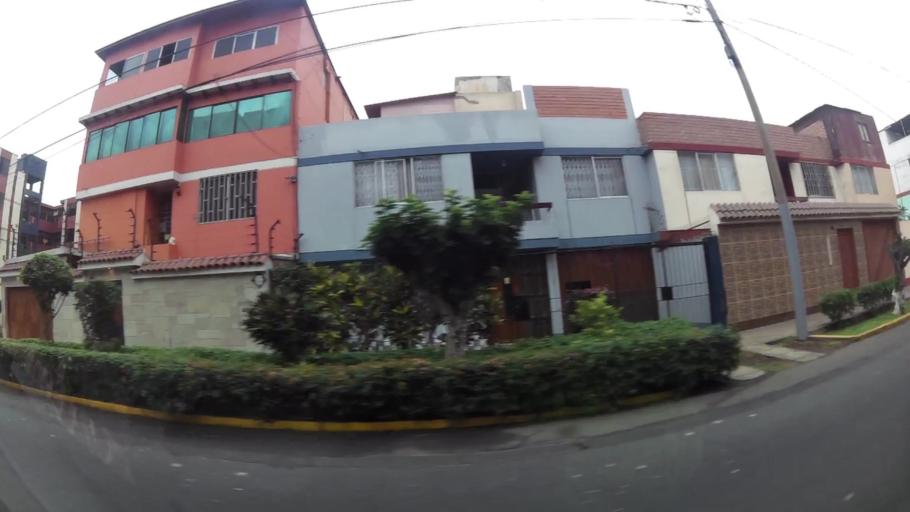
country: PE
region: Lima
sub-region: Lima
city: San Isidro
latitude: -12.0914
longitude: -77.0810
